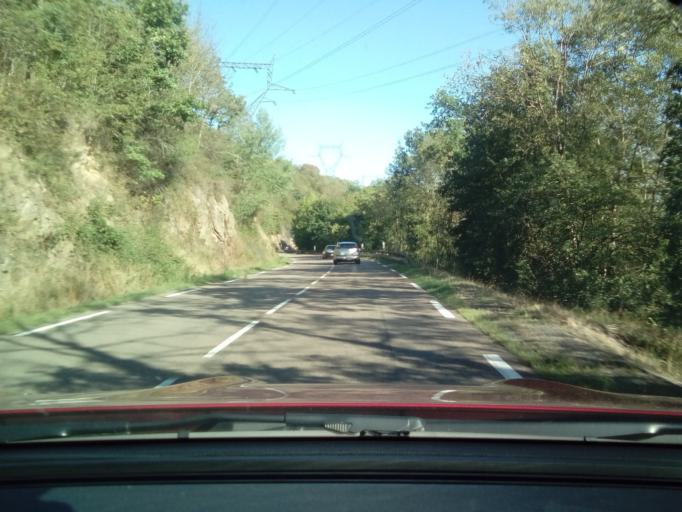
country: FR
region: Rhone-Alpes
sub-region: Departement du Rhone
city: Saint-Verand
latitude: 45.9081
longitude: 4.5181
